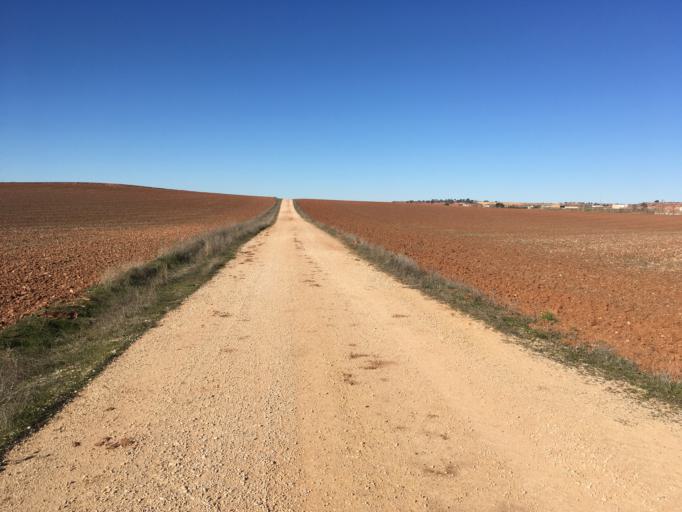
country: ES
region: Castille-La Mancha
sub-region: Provincia de Cuenca
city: Atalaya del Canavate
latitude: 39.5407
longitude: -2.2414
